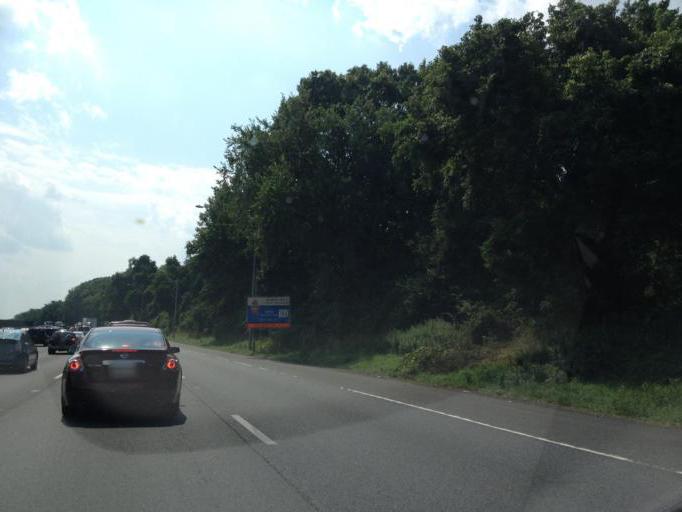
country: US
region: Maryland
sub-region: Montgomery County
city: Hillandale
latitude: 39.0200
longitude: -76.9840
